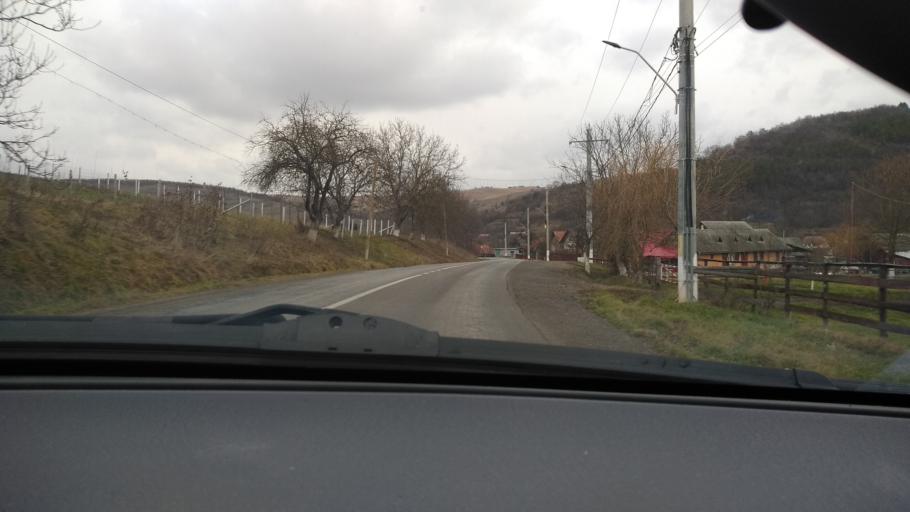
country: RO
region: Mures
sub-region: Comuna Pasareni
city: Pasareni
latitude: 46.5397
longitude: 24.6935
